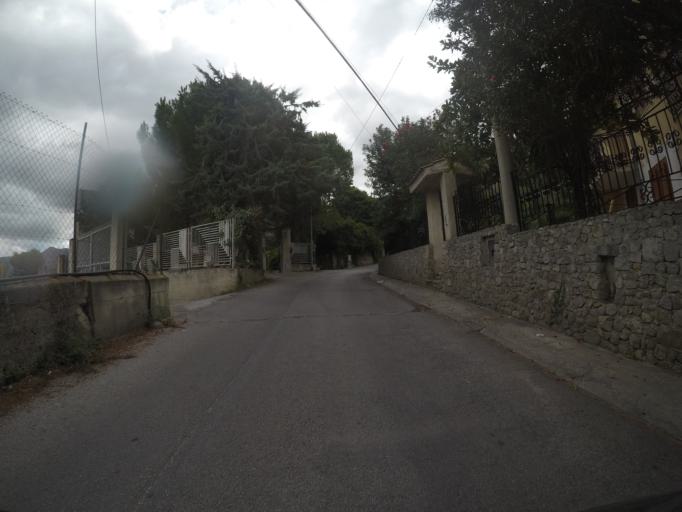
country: IT
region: Sicily
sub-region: Palermo
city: Carini
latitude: 38.1253
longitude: 13.1827
